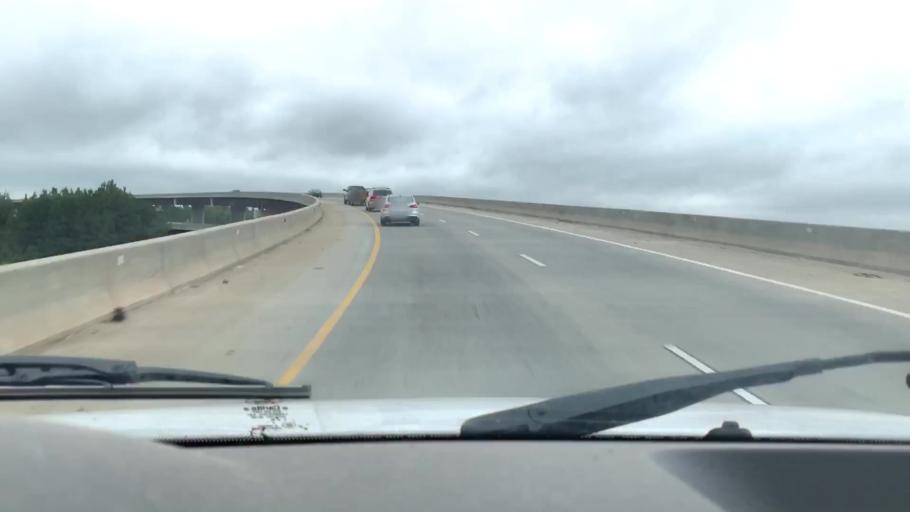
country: US
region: North Carolina
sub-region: Mecklenburg County
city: Huntersville
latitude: 35.3654
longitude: -80.8429
